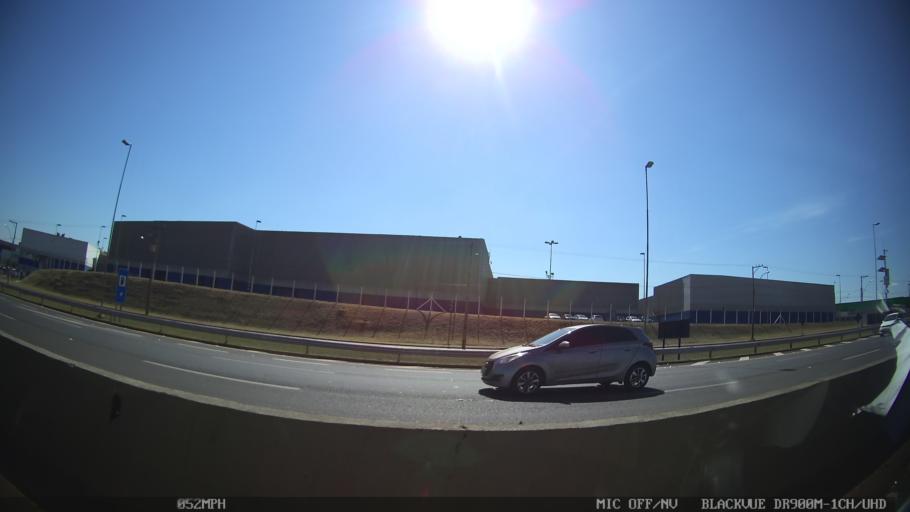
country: BR
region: Sao Paulo
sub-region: Ribeirao Preto
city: Ribeirao Preto
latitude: -21.2084
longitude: -47.7646
